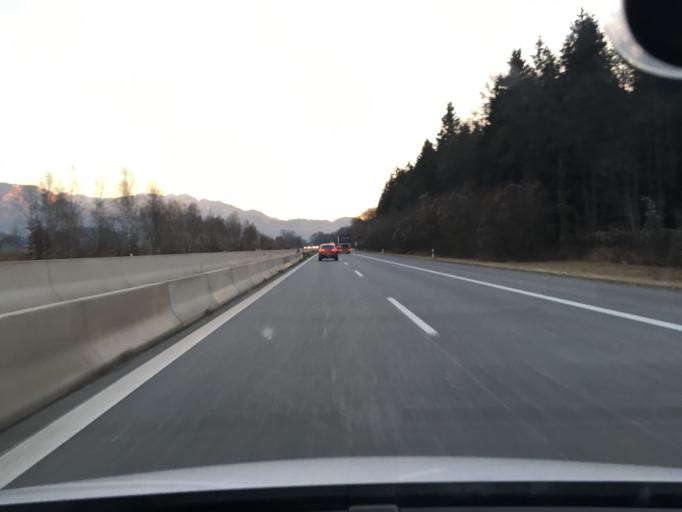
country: AT
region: Tyrol
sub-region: Politischer Bezirk Kufstein
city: Erl
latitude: 47.6930
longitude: 12.1627
